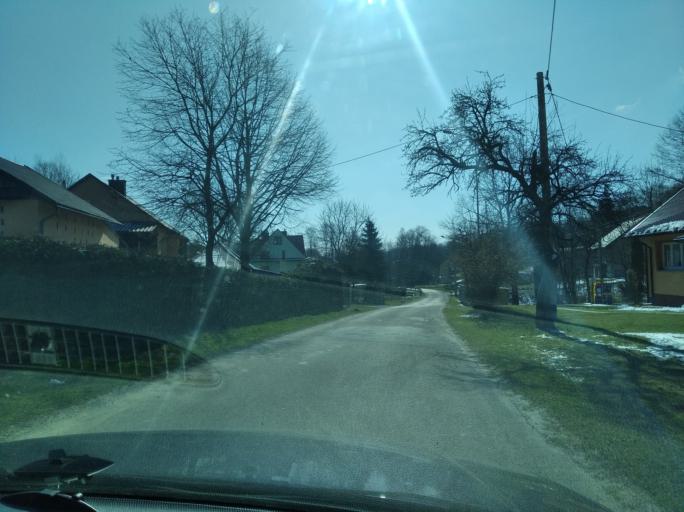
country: PL
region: Subcarpathian Voivodeship
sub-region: Powiat strzyzowski
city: Jawornik
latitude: 49.8512
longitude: 21.8698
